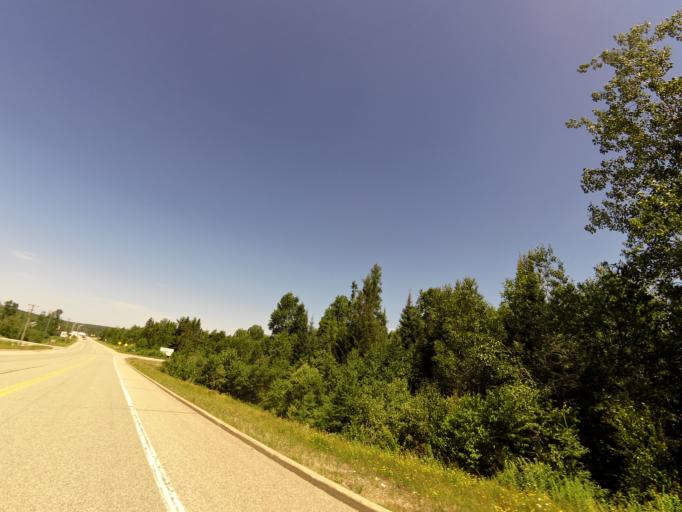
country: CA
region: Quebec
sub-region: Abitibi-Temiscamingue
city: Temiscaming
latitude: 46.7334
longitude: -79.0623
